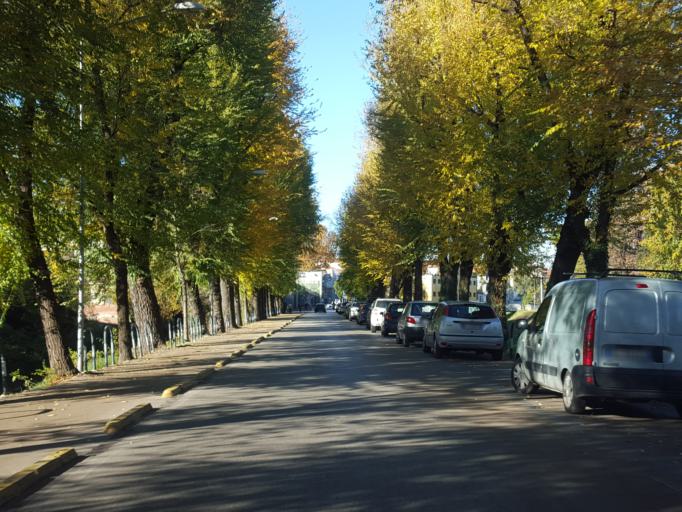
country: IT
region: Veneto
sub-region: Provincia di Vicenza
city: Vicenza
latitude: 45.5462
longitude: 11.5520
